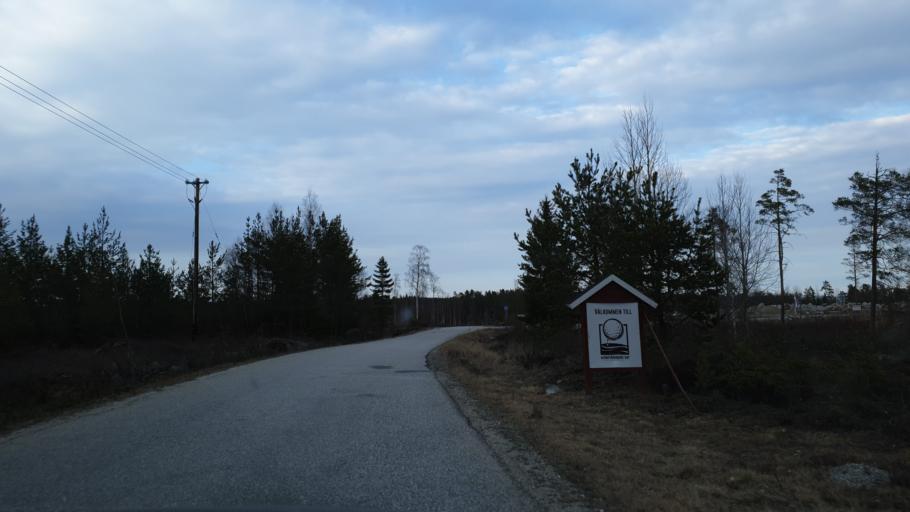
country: SE
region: Vaesternorrland
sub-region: Sundsvalls Kommun
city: Njurundabommen
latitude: 62.0161
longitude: 17.4020
